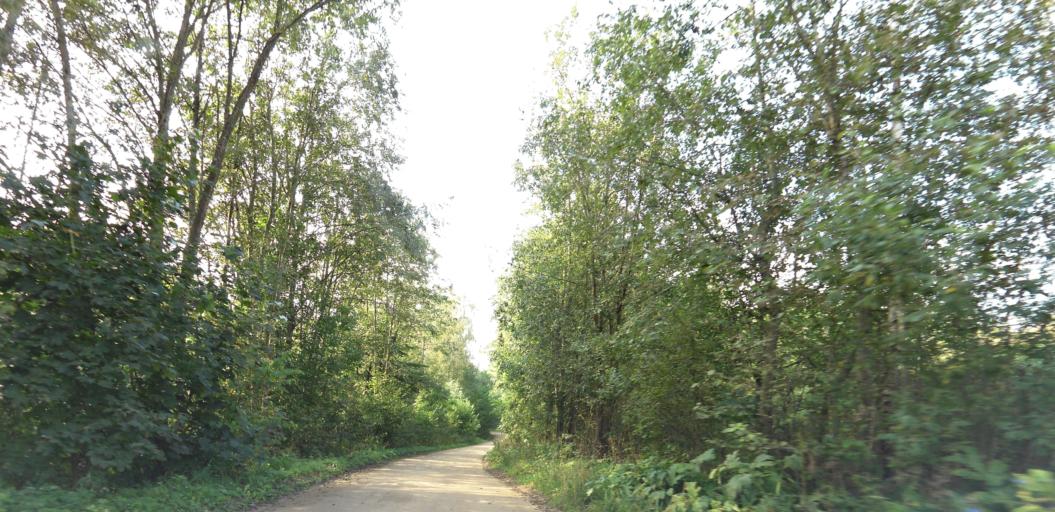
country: LT
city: Grigiskes
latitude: 54.7733
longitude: 25.0606
